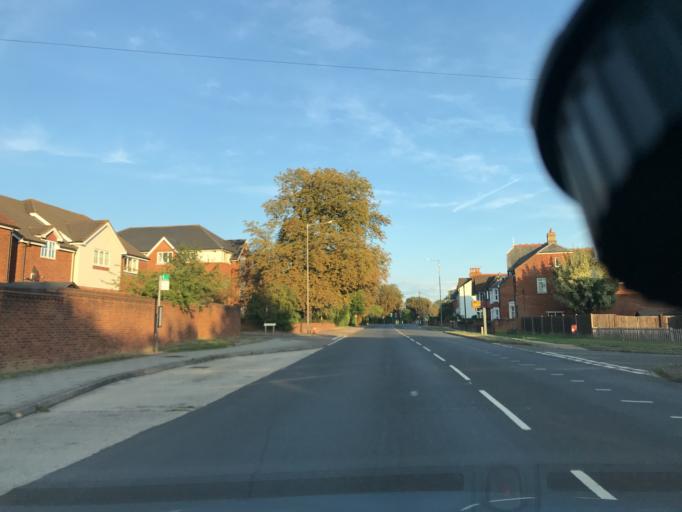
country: GB
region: England
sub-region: Buckinghamshire
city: Aylesbury
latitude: 51.8087
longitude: -0.8023
